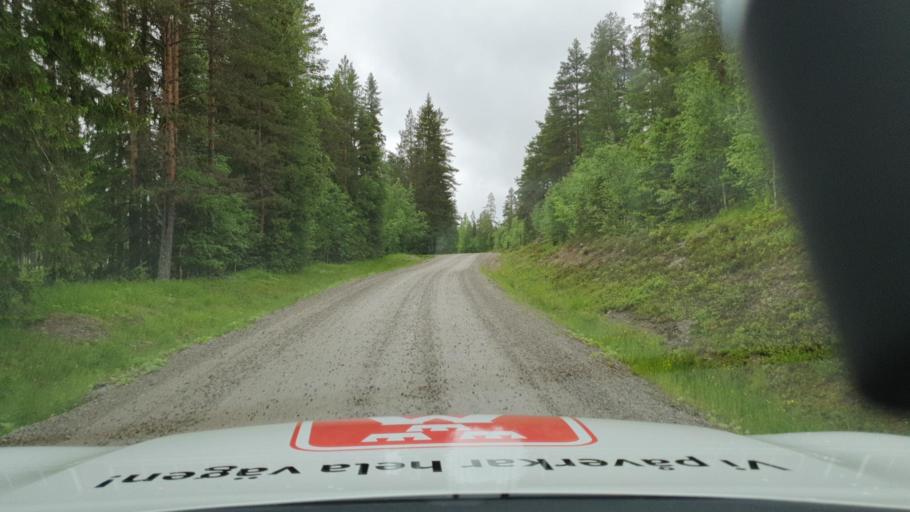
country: SE
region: Vaesterbotten
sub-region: Dorotea Kommun
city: Dorotea
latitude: 64.0355
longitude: 16.7591
